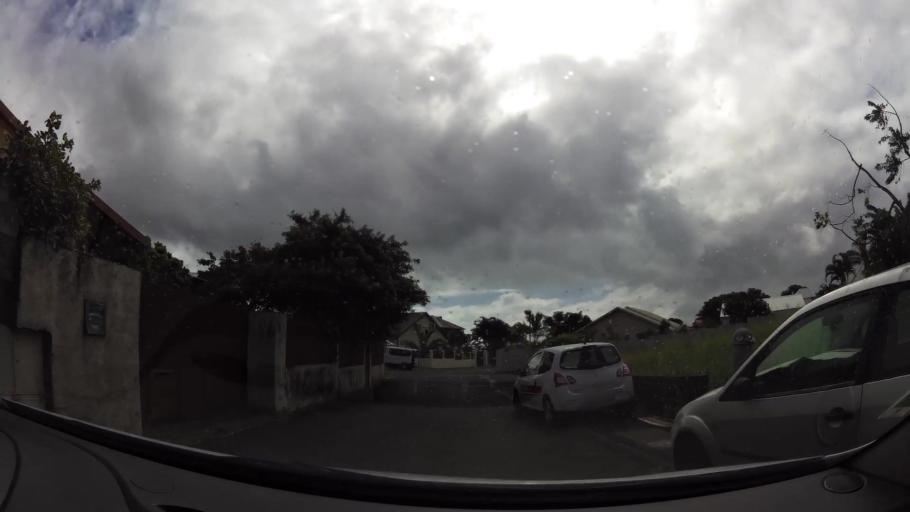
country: RE
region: Reunion
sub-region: Reunion
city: Sainte-Marie
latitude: -20.8963
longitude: 55.5644
